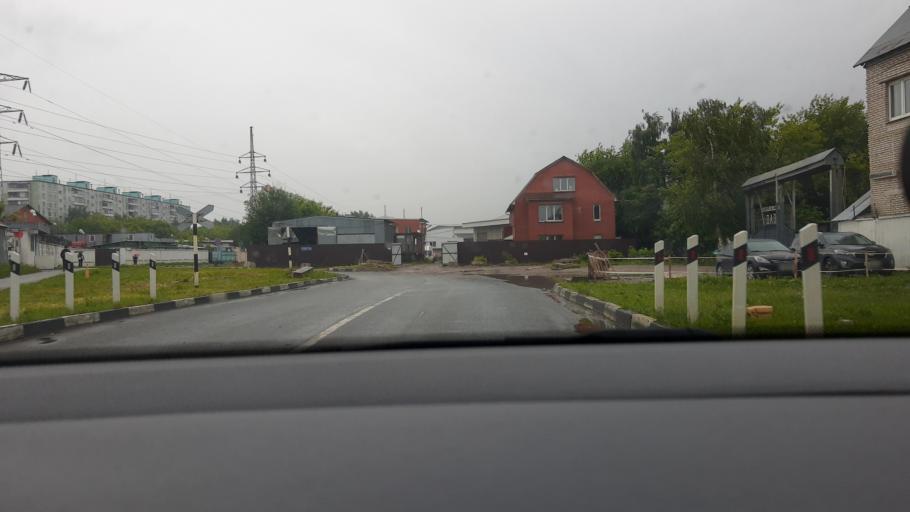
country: RU
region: Moskovskaya
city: Lyubertsy
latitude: 55.6635
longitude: 37.8937
